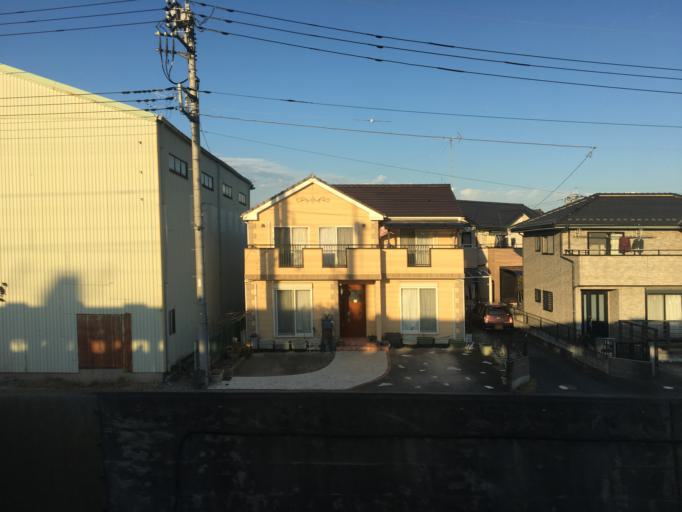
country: JP
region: Gunma
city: Maebashi-shi
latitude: 36.3782
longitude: 139.0966
